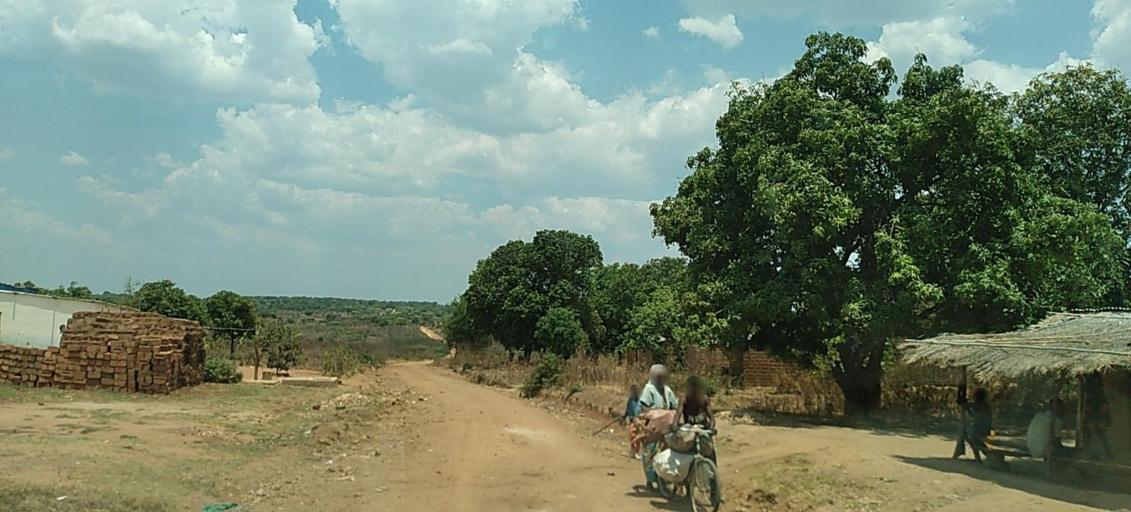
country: ZM
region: Copperbelt
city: Luanshya
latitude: -13.3699
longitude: 28.4143
